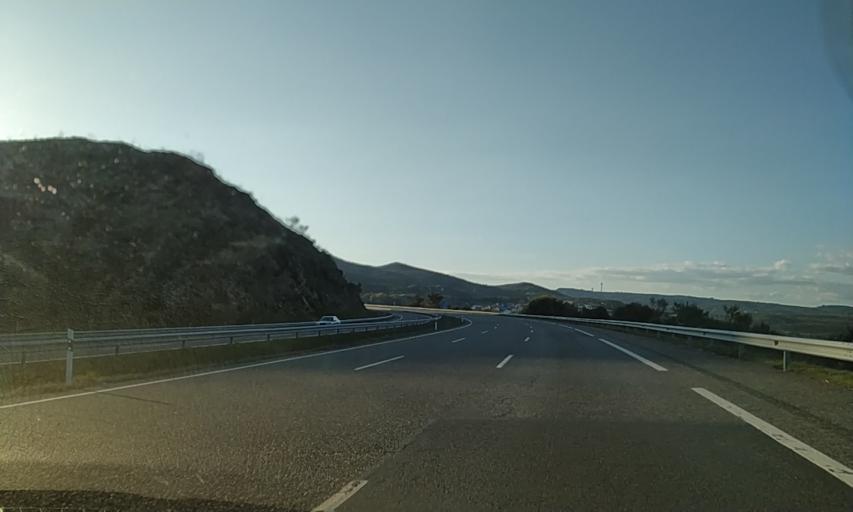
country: ES
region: Galicia
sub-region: Provincia de Ourense
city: Verin
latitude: 41.9625
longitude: -7.5168
